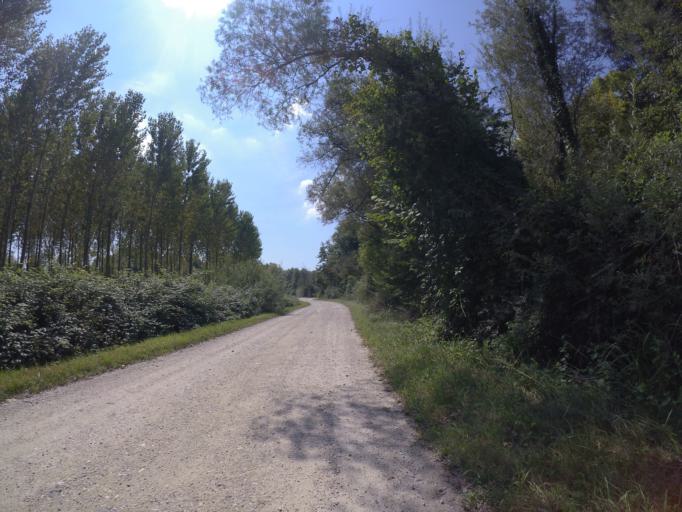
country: IT
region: Friuli Venezia Giulia
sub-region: Provincia di Udine
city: Bertiolo
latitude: 45.9153
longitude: 13.0619
